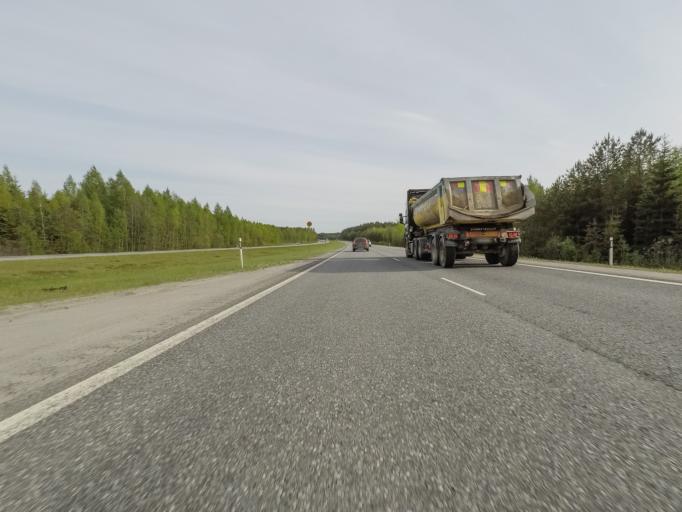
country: FI
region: Haeme
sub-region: Haemeenlinna
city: Haemeenlinna
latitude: 60.9326
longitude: 24.5174
